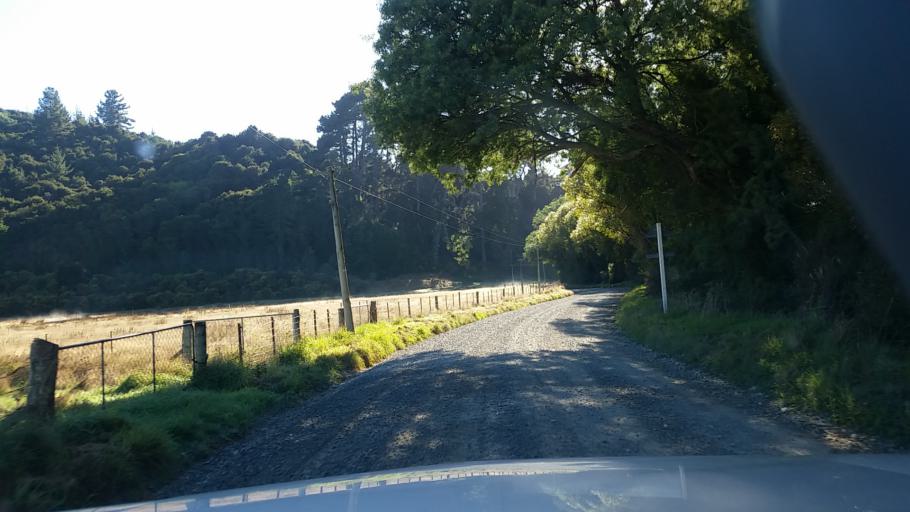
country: NZ
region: Marlborough
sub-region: Marlborough District
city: Blenheim
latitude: -41.4516
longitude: 173.8714
